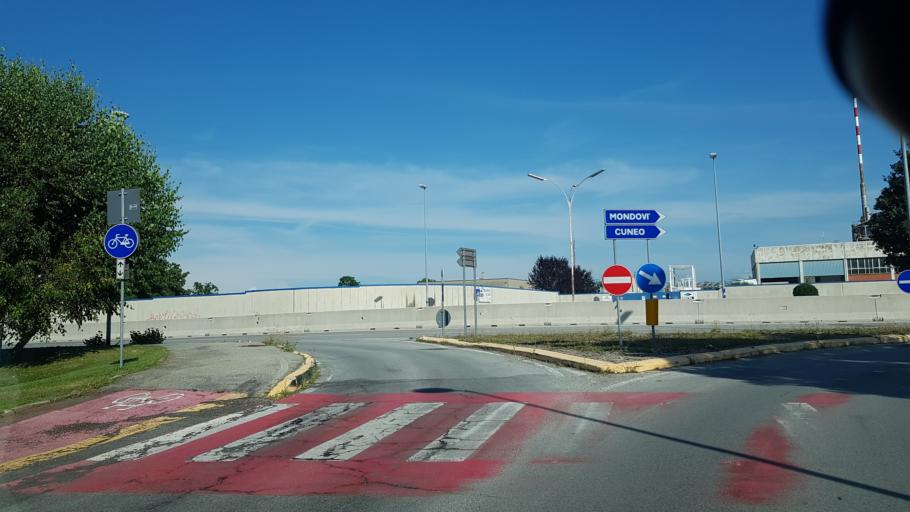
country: IT
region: Piedmont
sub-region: Provincia di Cuneo
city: Cuneo
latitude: 44.3914
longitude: 7.5843
